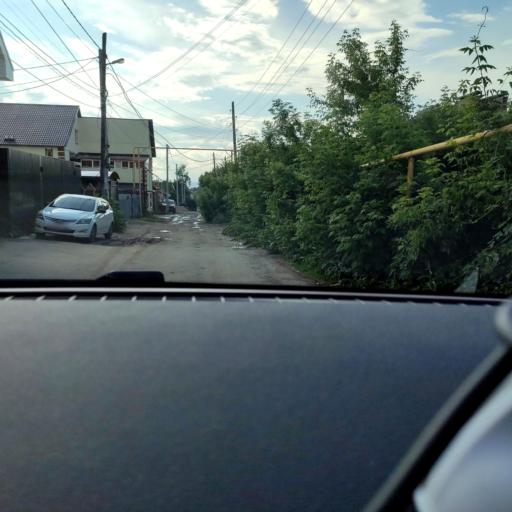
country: RU
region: Samara
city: Samara
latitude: 53.2683
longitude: 50.2077
